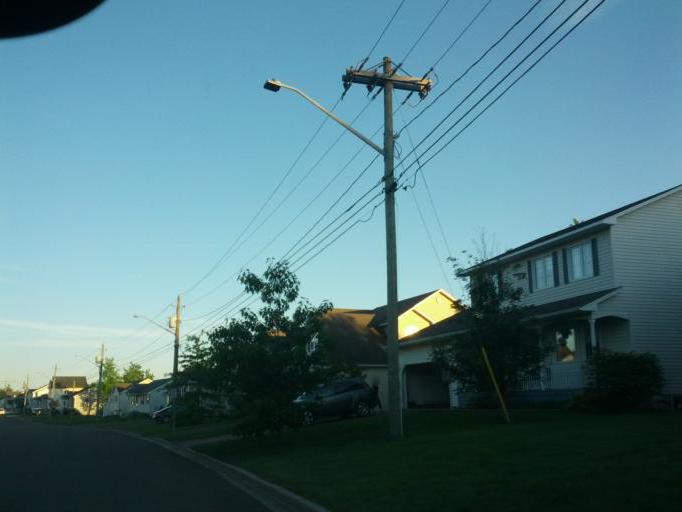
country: CA
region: New Brunswick
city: Moncton
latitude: 46.1151
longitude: -64.8678
